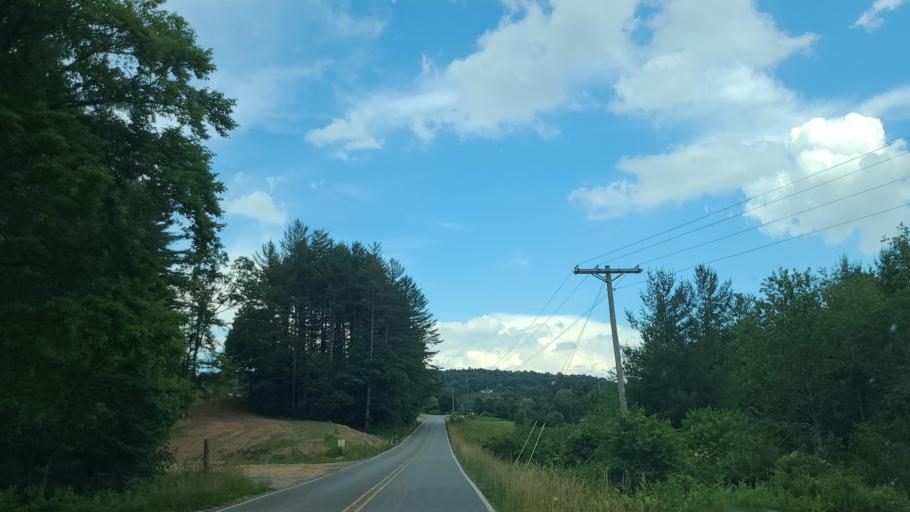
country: US
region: North Carolina
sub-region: Ashe County
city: Jefferson
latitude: 36.3894
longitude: -81.3569
